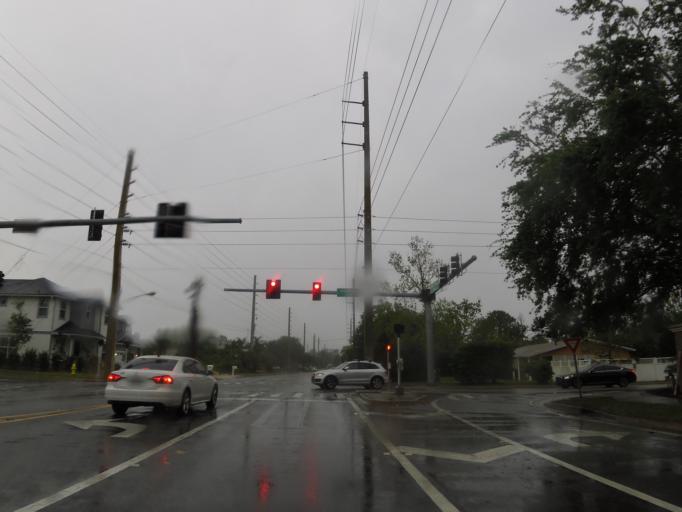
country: US
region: Florida
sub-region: Duval County
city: Jacksonville Beach
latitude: 30.2673
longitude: -81.3947
